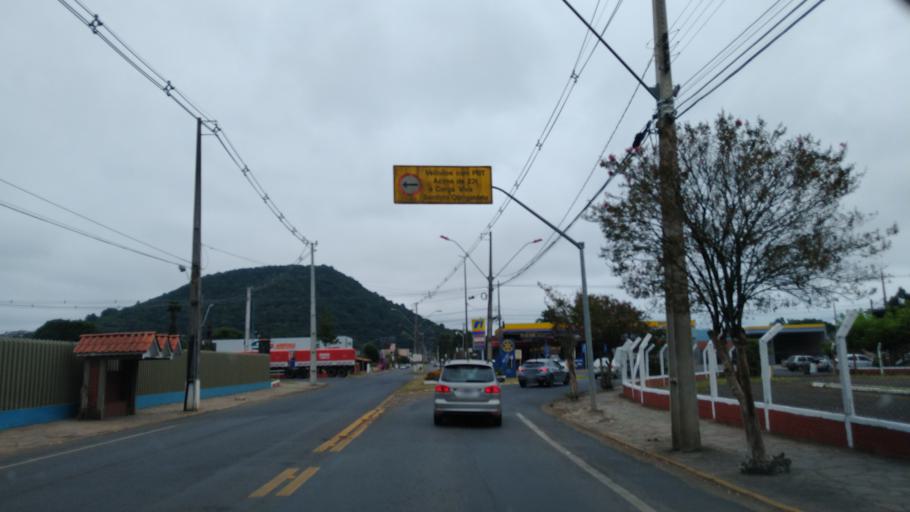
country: BR
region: Santa Catarina
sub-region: Porto Uniao
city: Porto Uniao
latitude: -26.2569
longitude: -51.0675
